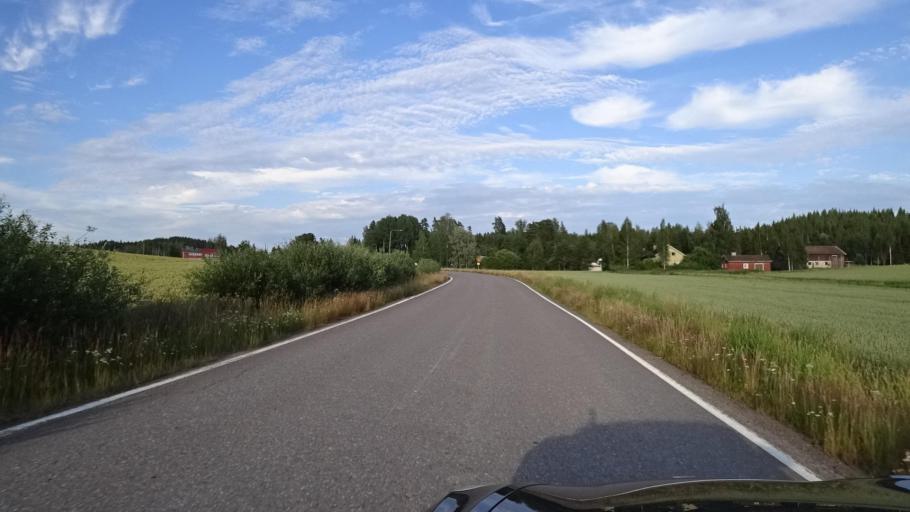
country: FI
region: Uusimaa
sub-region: Helsinki
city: Saukkola
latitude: 60.4003
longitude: 24.0609
